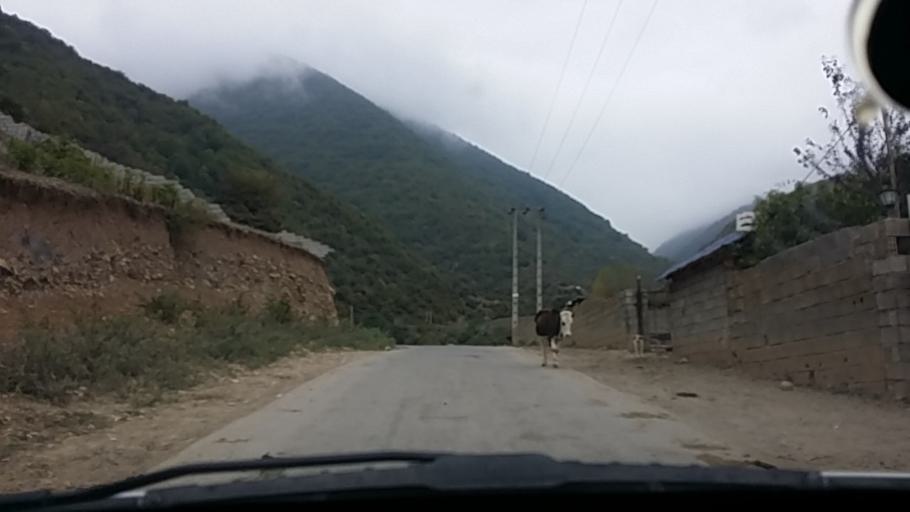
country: IR
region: Mazandaran
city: `Abbasabad
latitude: 36.4688
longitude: 51.1396
